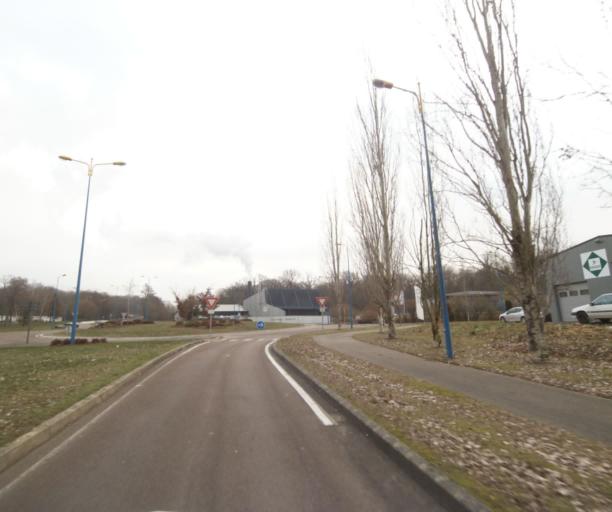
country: FR
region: Champagne-Ardenne
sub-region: Departement de la Haute-Marne
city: Bettancourt-la-Ferree
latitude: 48.6366
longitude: 4.9822
